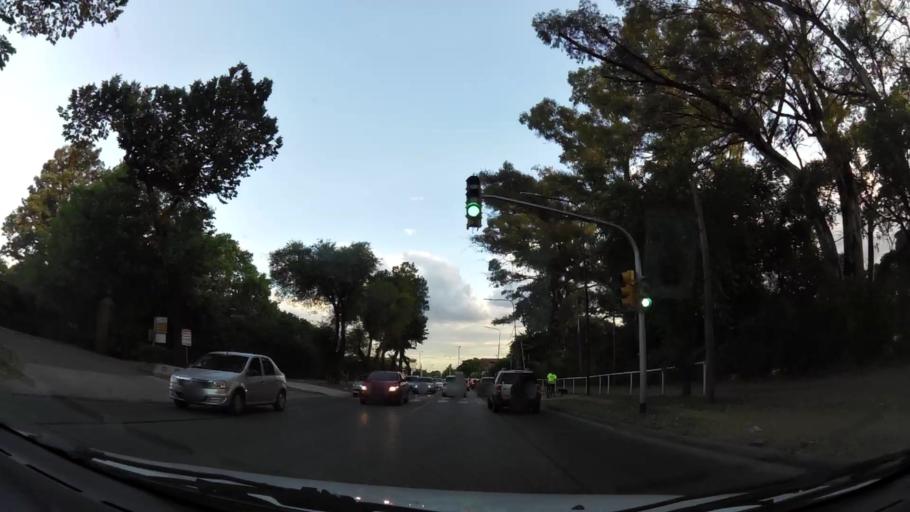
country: AR
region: Buenos Aires
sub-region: Partido de San Isidro
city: San Isidro
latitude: -34.4885
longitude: -58.5255
